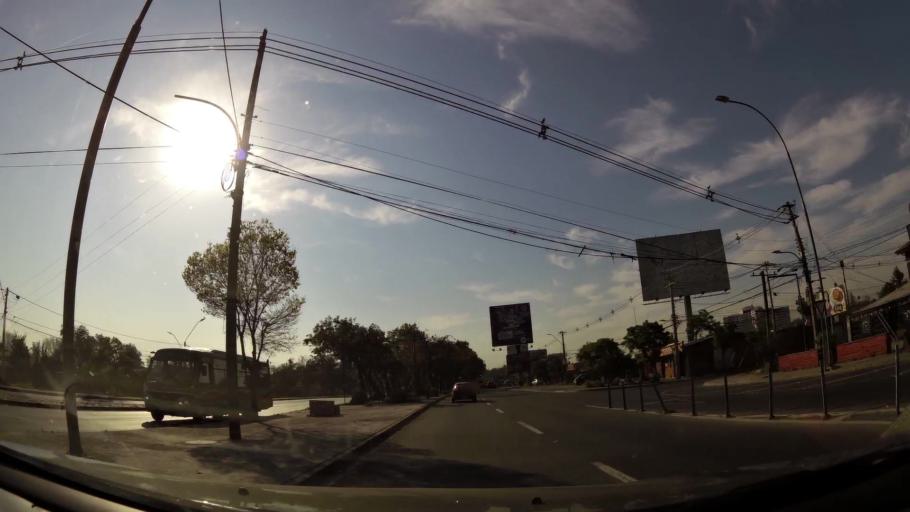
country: CL
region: Santiago Metropolitan
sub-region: Provincia de Maipo
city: San Bernardo
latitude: -33.5880
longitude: -70.7118
